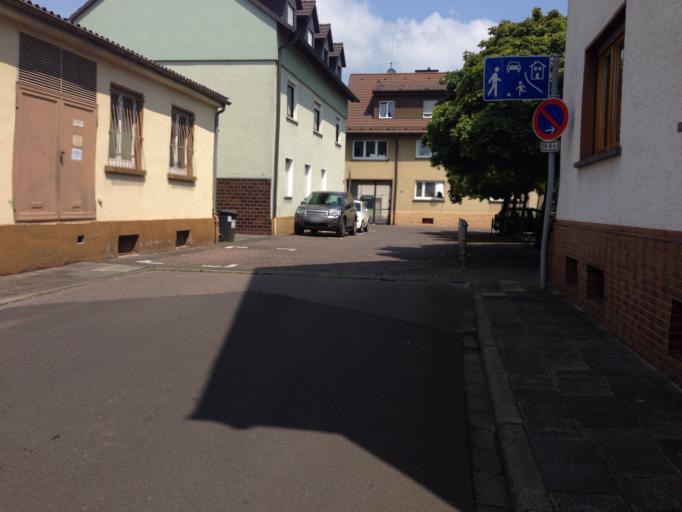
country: DE
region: Hesse
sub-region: Regierungsbezirk Darmstadt
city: Hanau am Main
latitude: 50.1000
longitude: 8.9292
